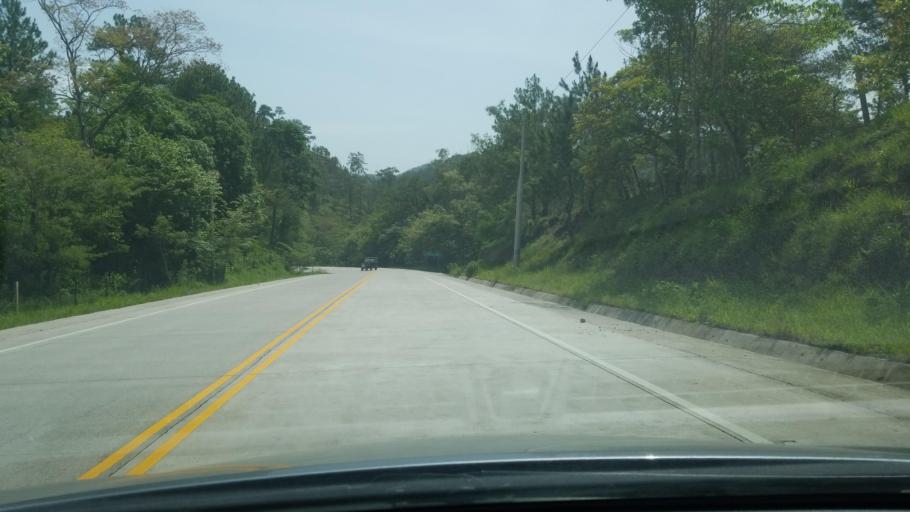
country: HN
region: Copan
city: Florida
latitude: 15.0111
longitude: -88.8349
